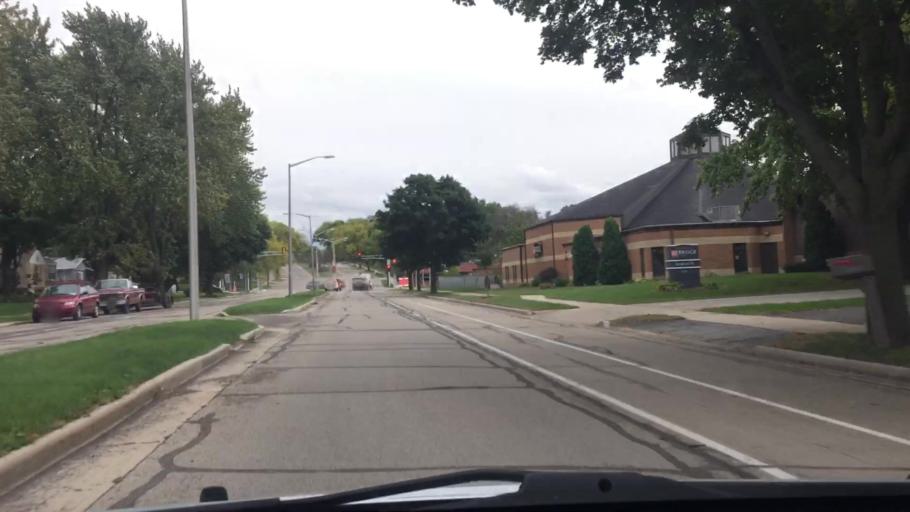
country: US
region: Wisconsin
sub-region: Waukesha County
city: Waukesha
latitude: 42.9897
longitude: -88.2322
